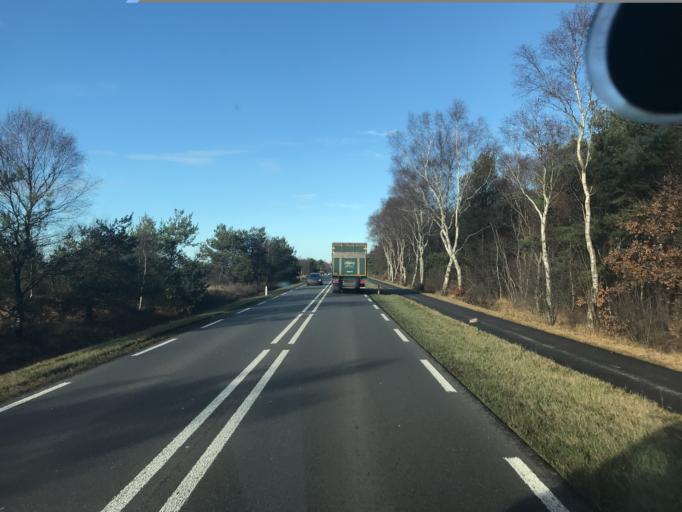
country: NL
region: Gelderland
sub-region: Gemeente Apeldoorn
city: Uddel
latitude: 52.2602
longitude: 5.7429
